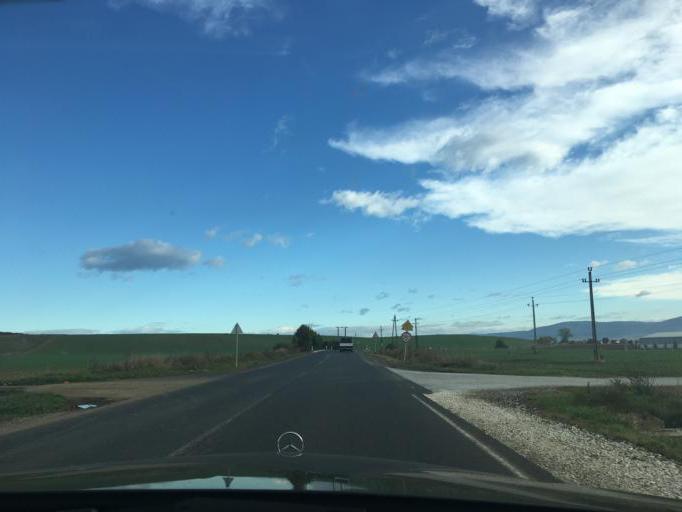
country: HU
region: Borsod-Abauj-Zemplen
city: Encs
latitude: 48.3535
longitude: 21.1271
